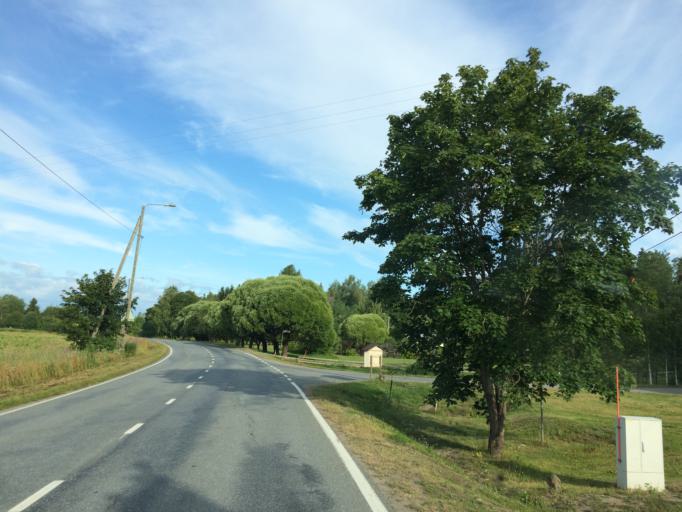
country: FI
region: Haeme
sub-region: Haemeenlinna
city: Janakkala
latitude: 60.9297
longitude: 24.5731
